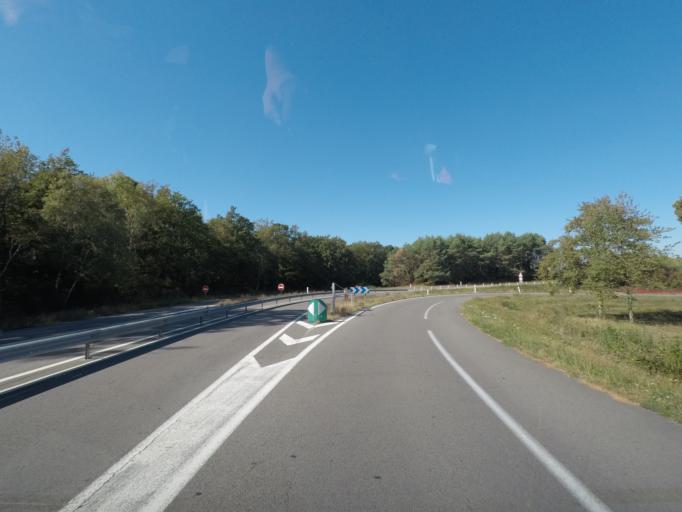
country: FR
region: Rhone-Alpes
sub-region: Departement de l'Ain
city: Attignat
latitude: 46.2603
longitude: 5.1646
